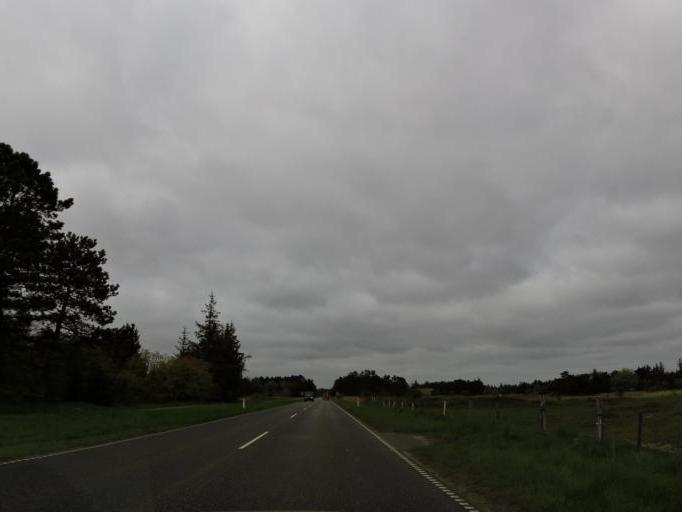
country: DE
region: Schleswig-Holstein
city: List
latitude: 55.1024
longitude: 8.5424
